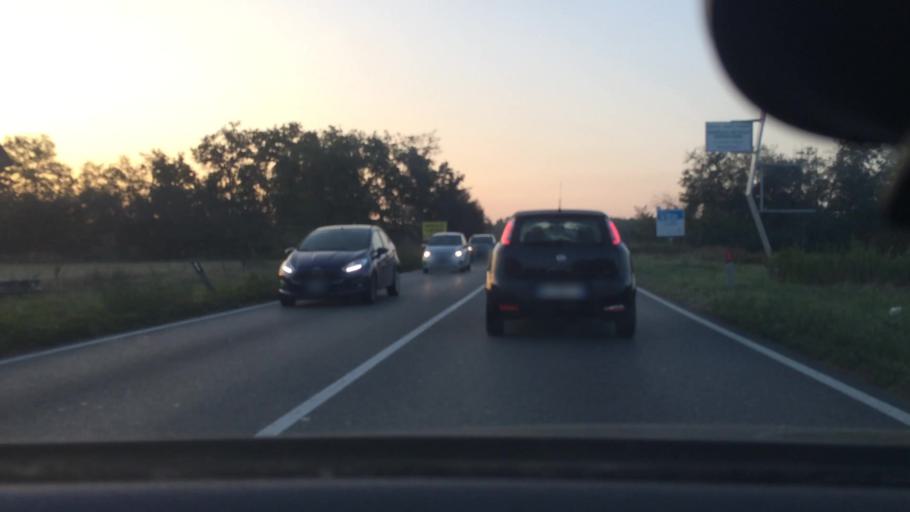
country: IT
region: Lombardy
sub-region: Citta metropolitana di Milano
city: Parabiago
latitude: 45.5381
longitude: 8.9630
